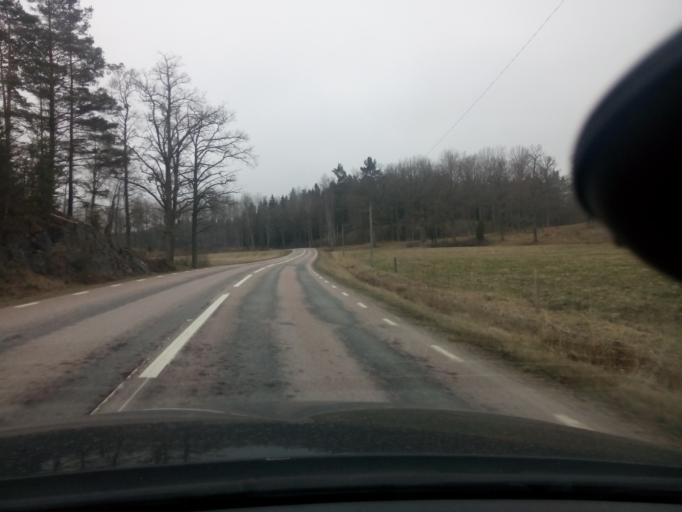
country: SE
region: Soedermanland
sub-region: Gnesta Kommun
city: Gnesta
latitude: 59.0320
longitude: 17.1650
